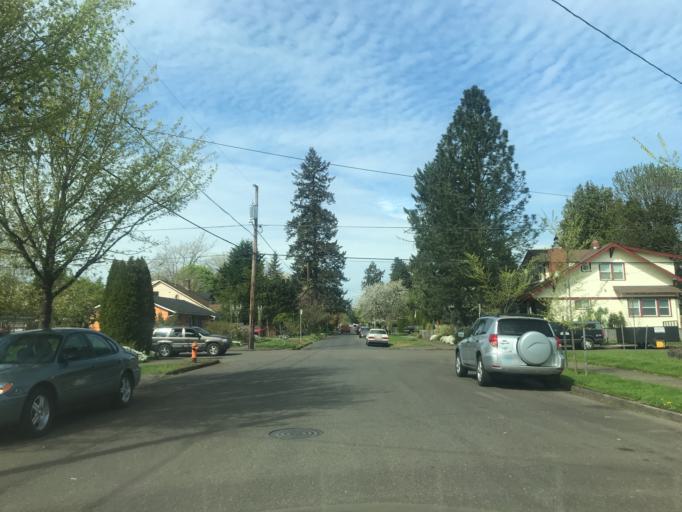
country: US
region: Oregon
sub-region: Multnomah County
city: Lents
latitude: 45.4801
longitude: -122.6017
